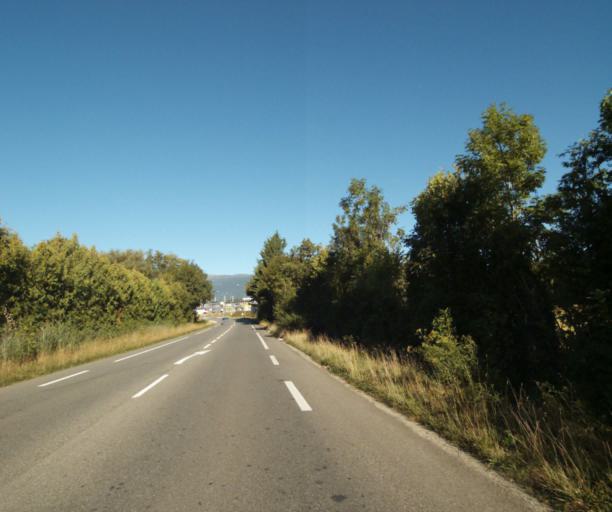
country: CH
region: Geneva
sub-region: Geneva
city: Meyrin
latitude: 46.2471
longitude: 6.0892
